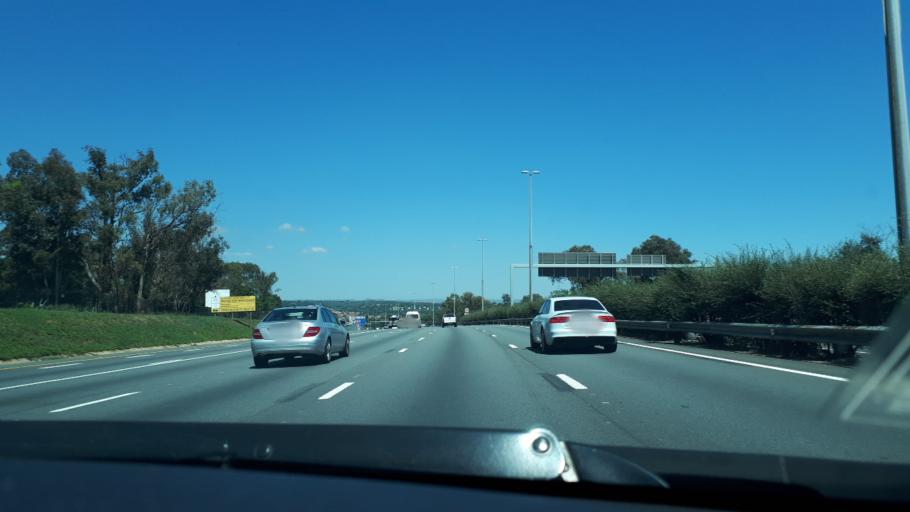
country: ZA
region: Gauteng
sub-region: City of Johannesburg Metropolitan Municipality
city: Midrand
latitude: -26.0432
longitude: 28.0880
